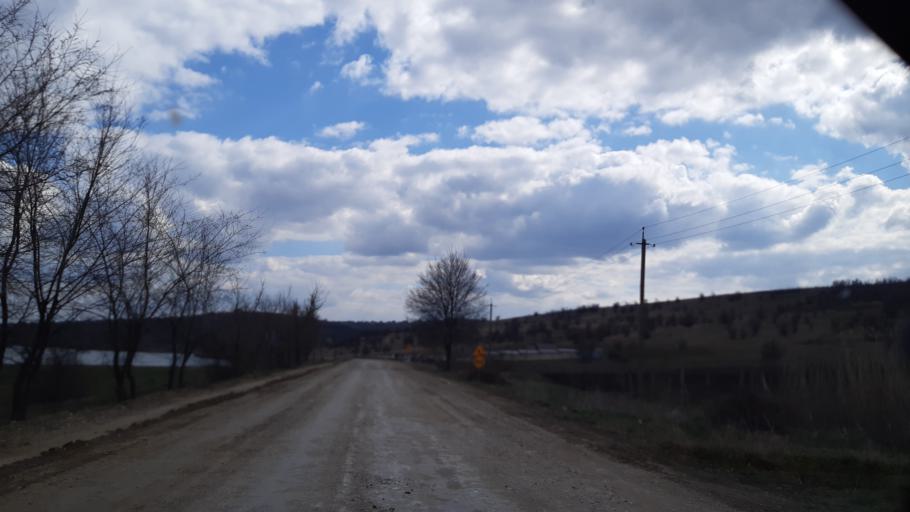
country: MD
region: Laloveni
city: Ialoveni
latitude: 46.8853
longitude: 28.7368
